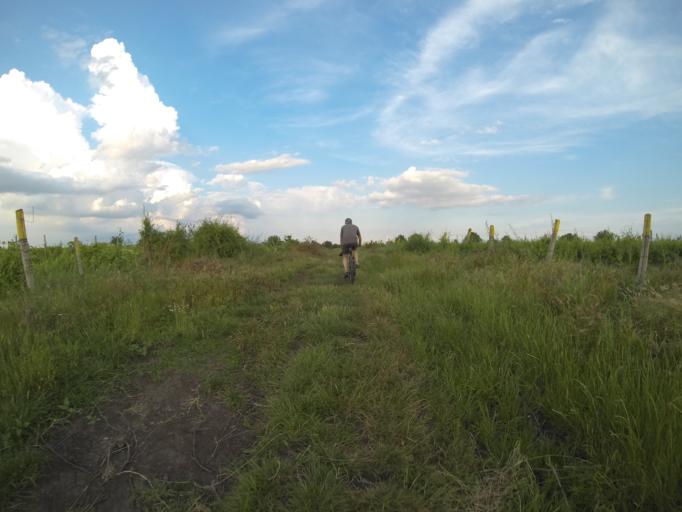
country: RO
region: Dolj
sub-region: Comuna Lipovu
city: Lipovu
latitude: 44.1144
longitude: 23.6785
